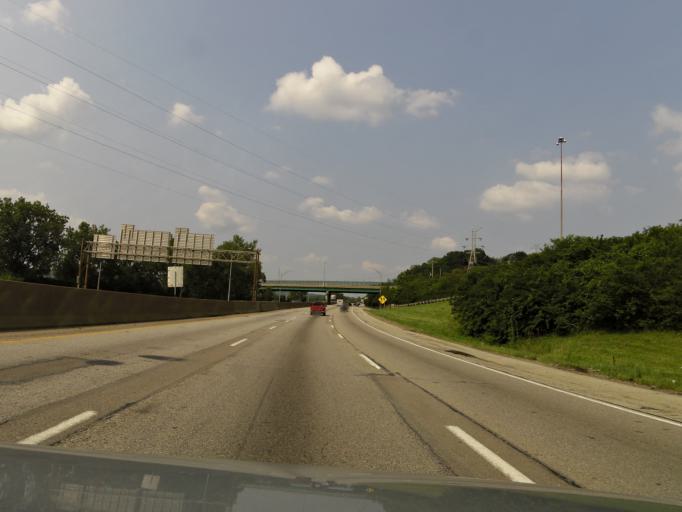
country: US
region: Ohio
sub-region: Hamilton County
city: Saint Bernard
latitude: 39.1523
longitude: -84.5396
